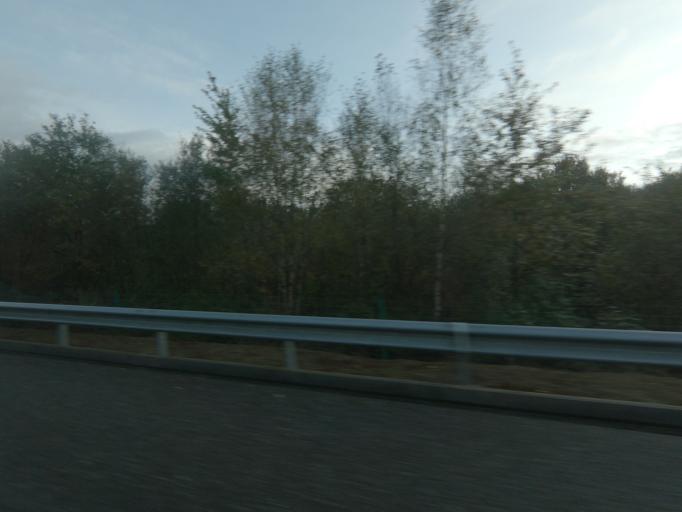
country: ES
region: Galicia
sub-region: Provincia de Pontevedra
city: Tui
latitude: 42.0909
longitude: -8.6422
